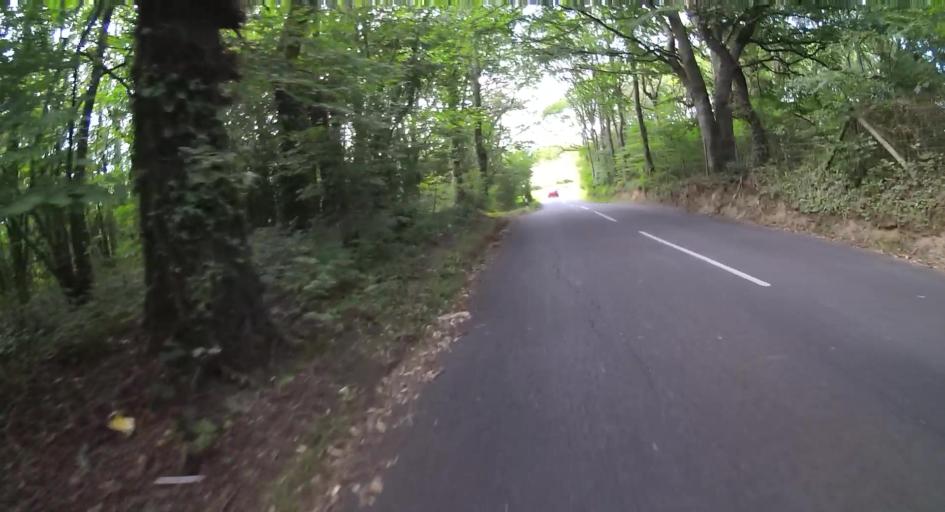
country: GB
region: England
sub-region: Isle of Wight
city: Newport
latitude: 50.6581
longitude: -1.2901
